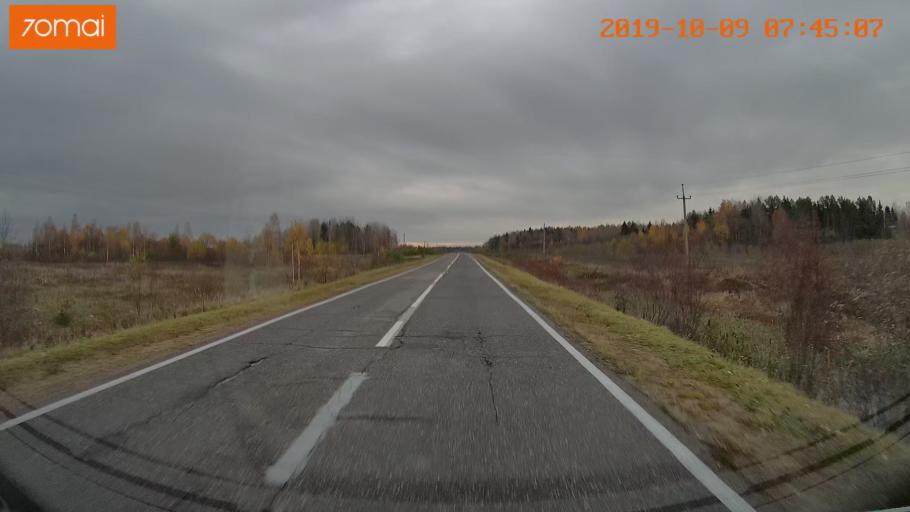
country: RU
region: Jaroslavl
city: Kukoboy
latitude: 58.6522
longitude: 39.7605
